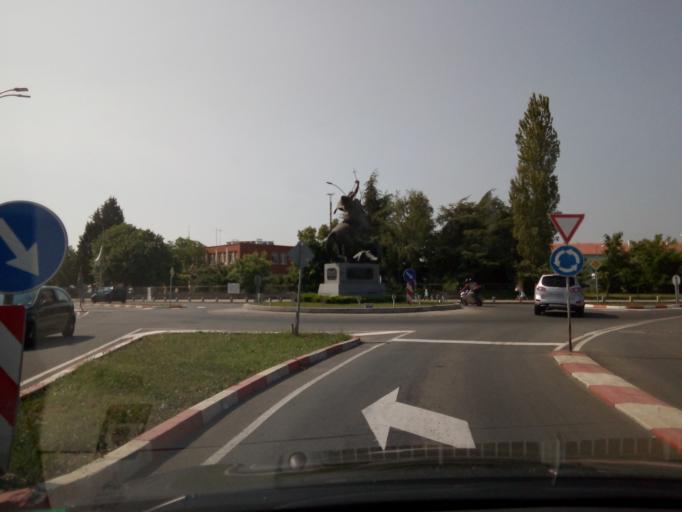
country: BG
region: Burgas
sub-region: Obshtina Pomorie
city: Pomorie
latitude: 42.5675
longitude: 27.6189
